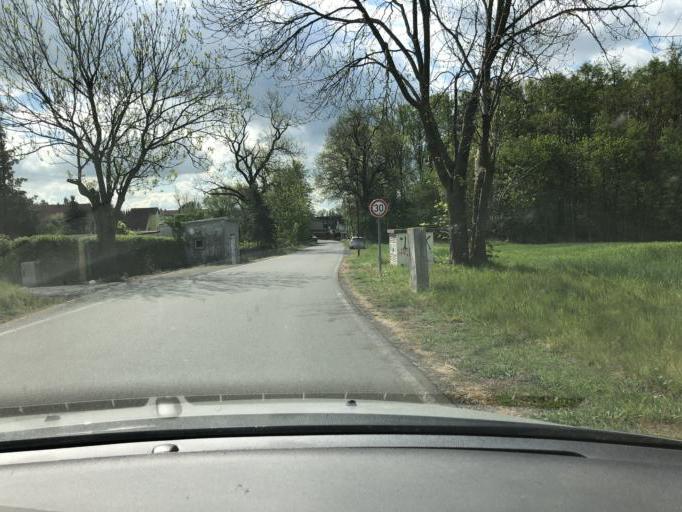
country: DE
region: Saxony
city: Grossposna
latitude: 51.2432
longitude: 12.4815
